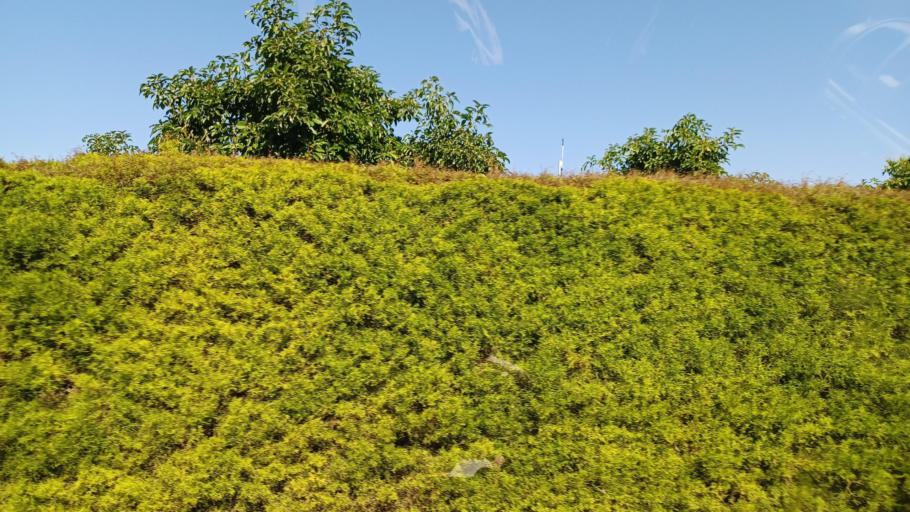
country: CY
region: Pafos
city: Pegeia
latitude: 34.8659
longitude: 32.3660
